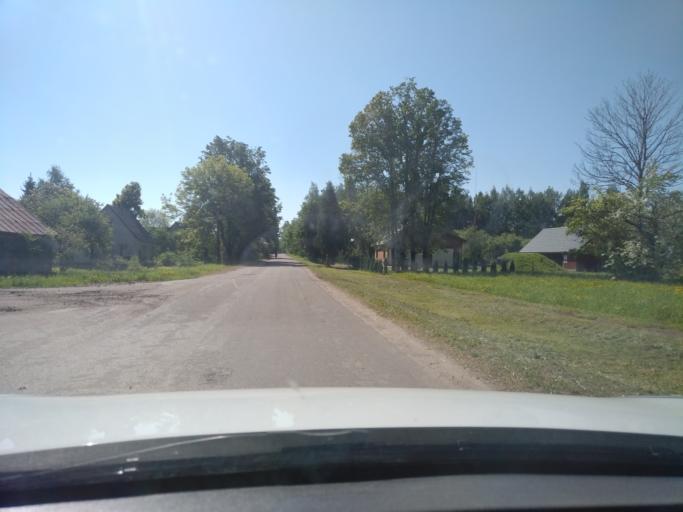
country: LT
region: Panevezys
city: Rokiskis
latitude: 55.7427
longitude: 25.5246
